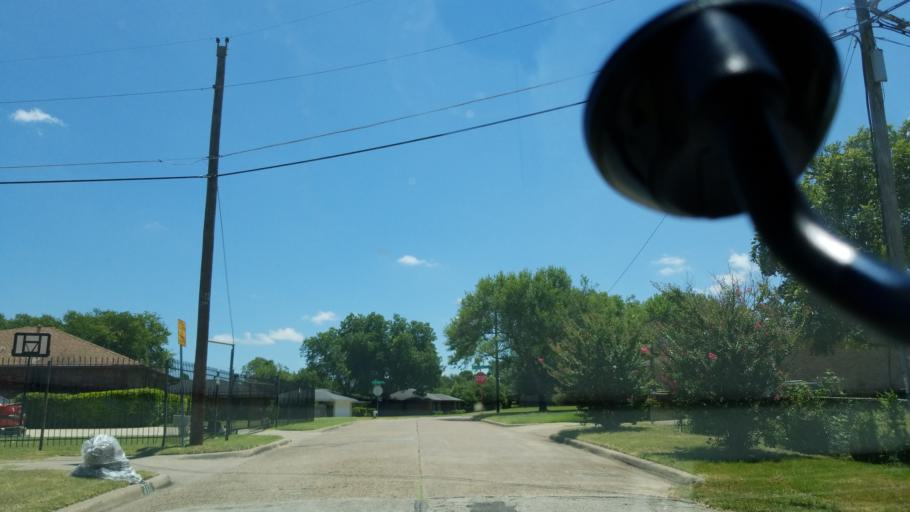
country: US
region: Texas
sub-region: Dallas County
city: Cockrell Hill
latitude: 32.6813
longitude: -96.8200
